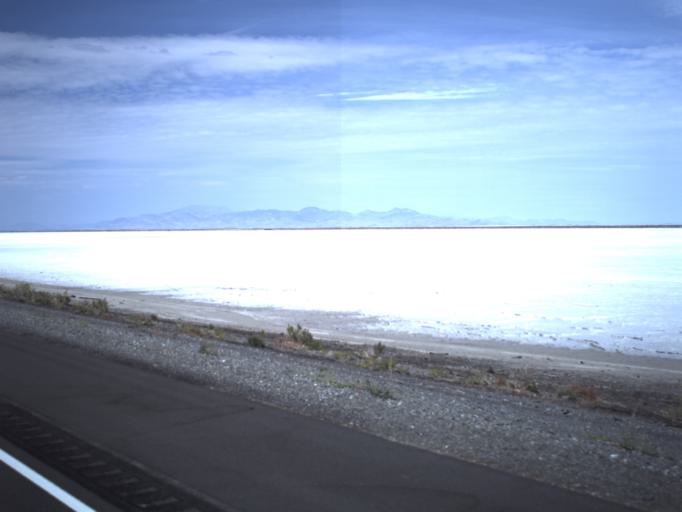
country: US
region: Utah
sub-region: Tooele County
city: Wendover
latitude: 40.7294
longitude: -113.3989
